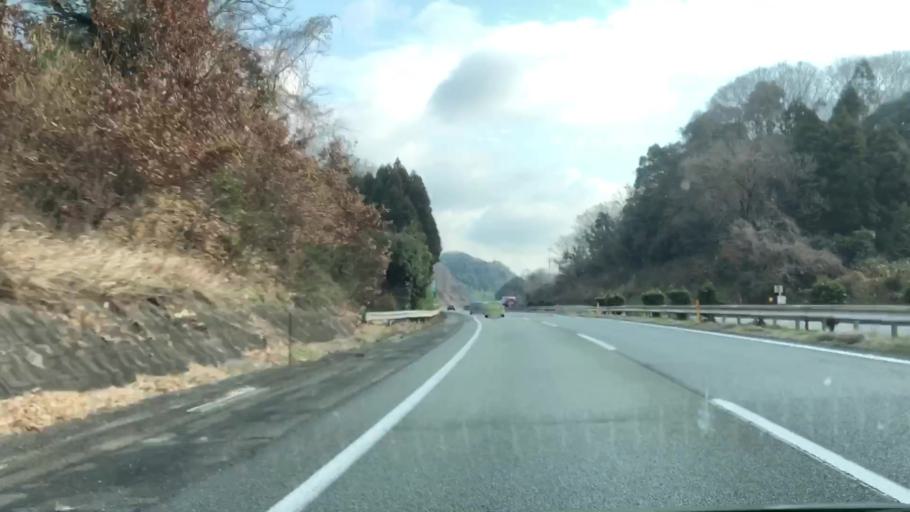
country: JP
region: Kumamoto
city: Tamana
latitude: 33.0028
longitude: 130.5856
